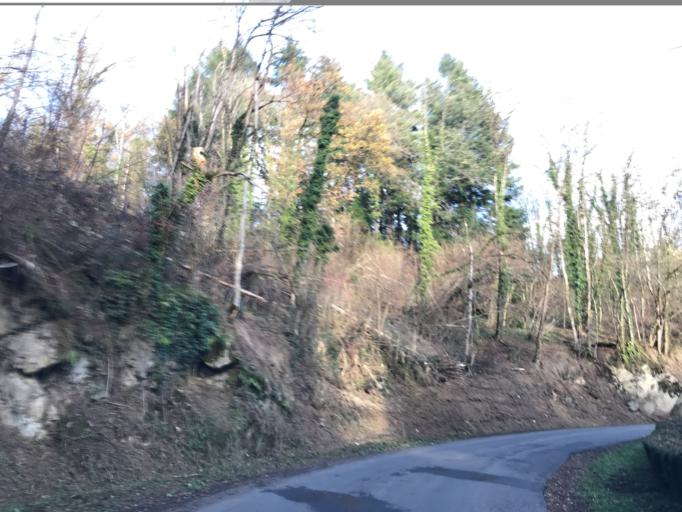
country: FR
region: Auvergne
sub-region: Departement du Puy-de-Dome
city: Courpiere
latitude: 45.7567
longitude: 3.6193
